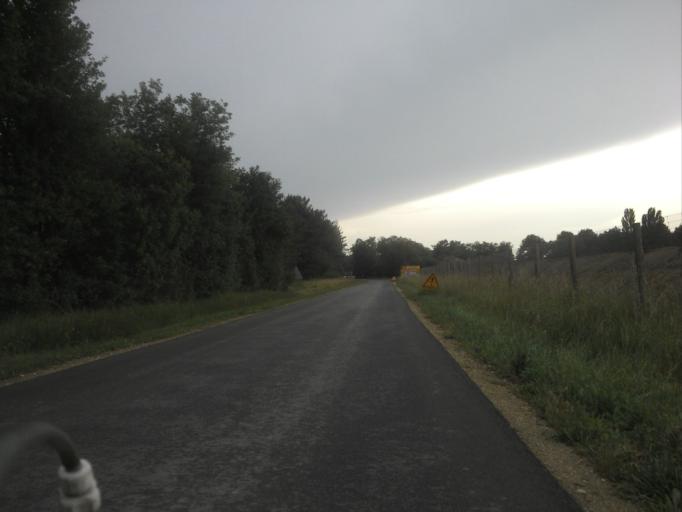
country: FR
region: Pays de la Loire
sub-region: Departement de Maine-et-Loire
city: Breze
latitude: 47.0957
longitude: -0.0011
